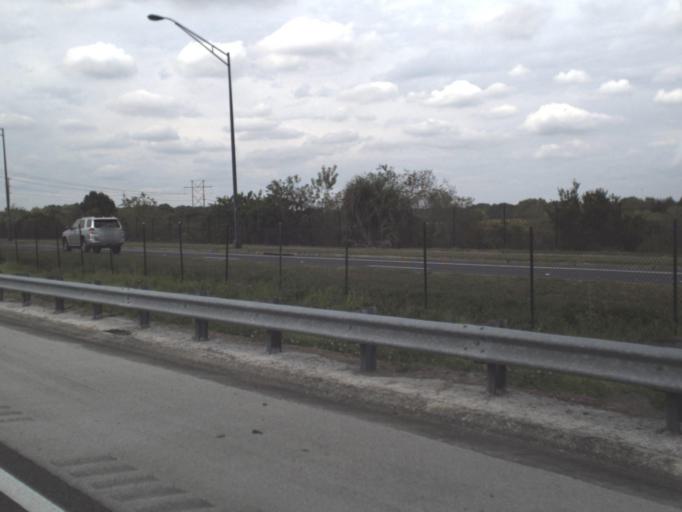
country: US
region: Florida
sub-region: Polk County
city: Medulla
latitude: 27.9974
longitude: -81.9867
